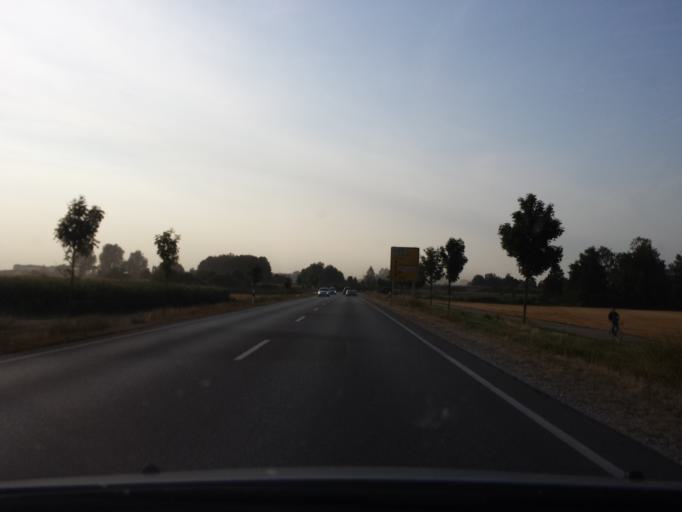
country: DE
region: Bavaria
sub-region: Swabia
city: Friedberg
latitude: 48.3907
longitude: 10.9514
